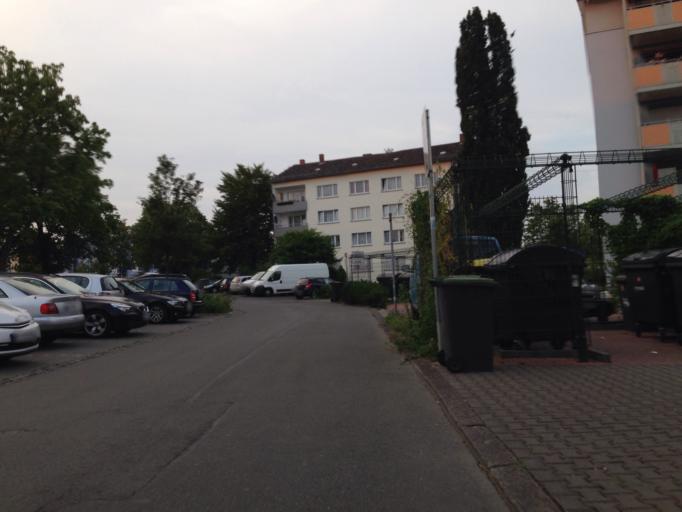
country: DE
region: Hesse
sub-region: Regierungsbezirk Giessen
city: Giessen
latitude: 50.5979
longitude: 8.6819
